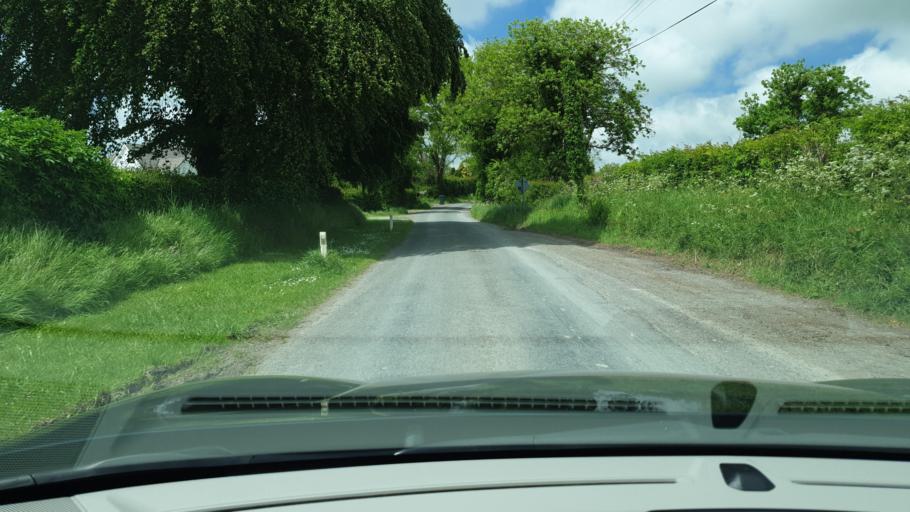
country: IE
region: Leinster
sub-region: An Mhi
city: Slane
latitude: 53.7319
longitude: -6.5500
